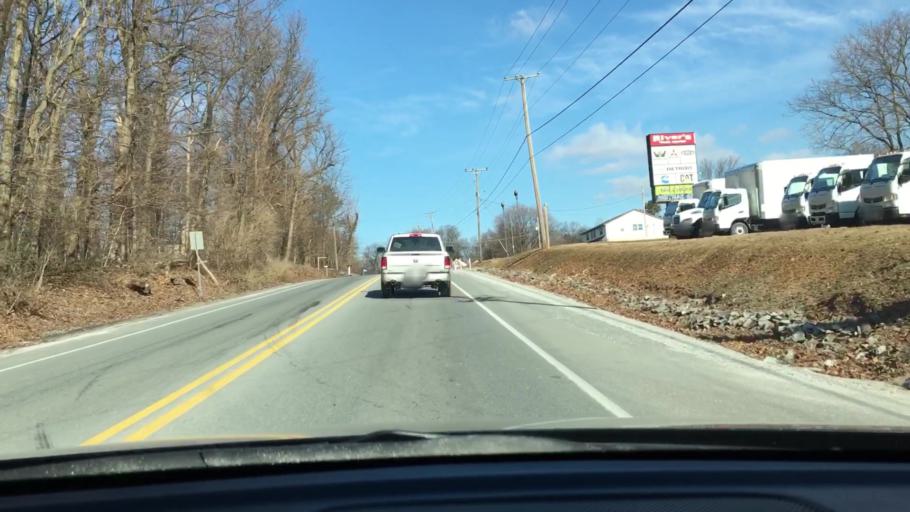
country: US
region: Pennsylvania
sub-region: York County
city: Yoe
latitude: 39.9267
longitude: -76.6370
